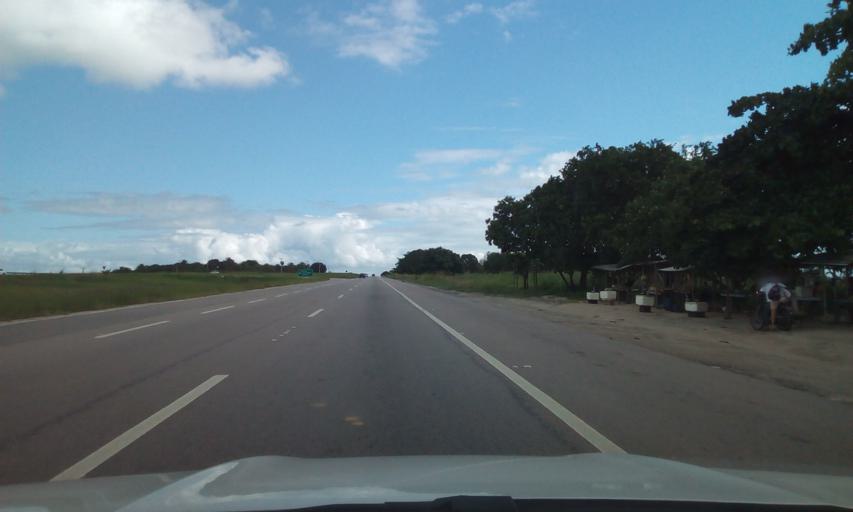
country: BR
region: Pernambuco
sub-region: Itapissuma
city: Itapissuma
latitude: -7.7012
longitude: -34.9231
